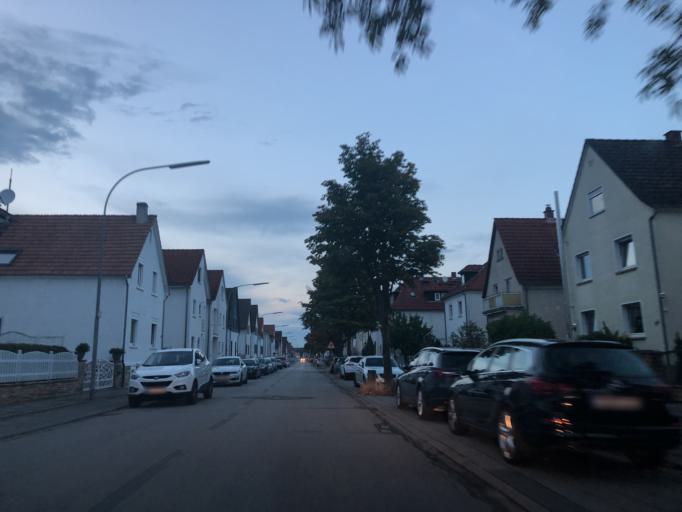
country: DE
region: Hesse
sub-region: Regierungsbezirk Darmstadt
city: Nauheim
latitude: 49.9586
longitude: 8.4503
